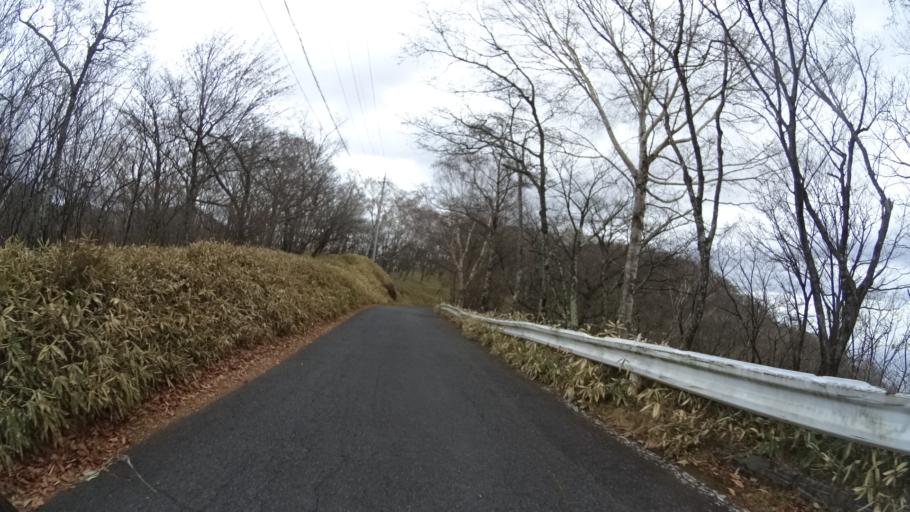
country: JP
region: Gunma
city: Omamacho-omama
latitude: 36.5252
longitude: 139.1770
